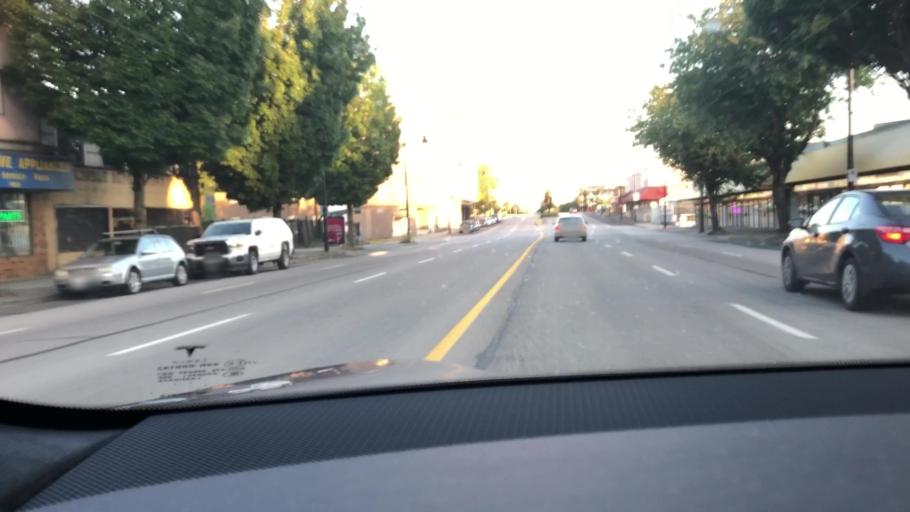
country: CA
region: British Columbia
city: Vancouver
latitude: 49.2476
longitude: -123.0703
